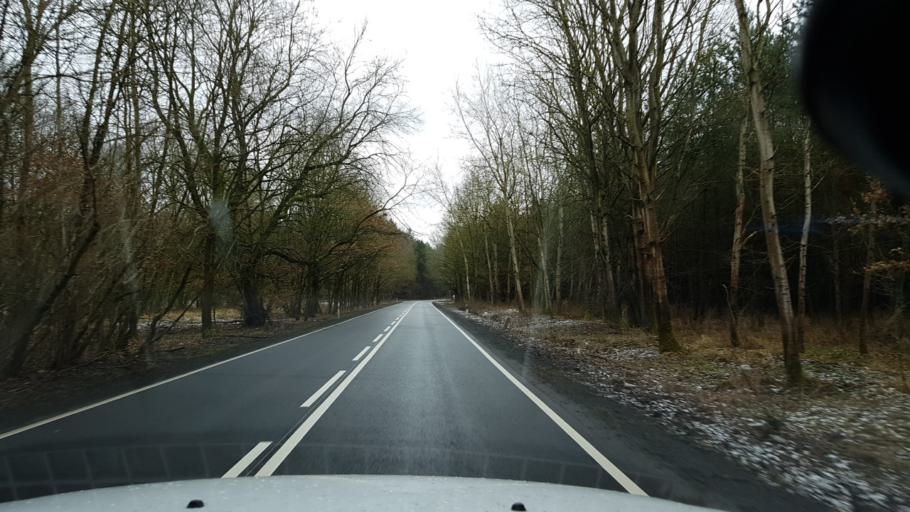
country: PL
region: West Pomeranian Voivodeship
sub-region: Powiat goleniowski
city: Stepnica
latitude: 53.6431
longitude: 14.6587
